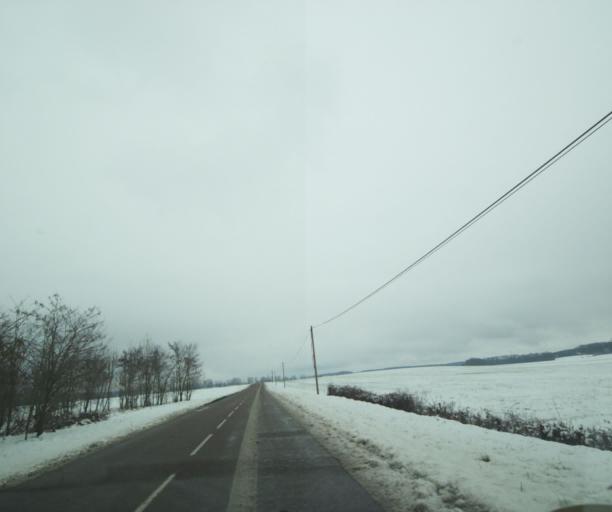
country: FR
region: Champagne-Ardenne
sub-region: Departement de la Haute-Marne
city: Montier-en-Der
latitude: 48.4506
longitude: 4.7793
